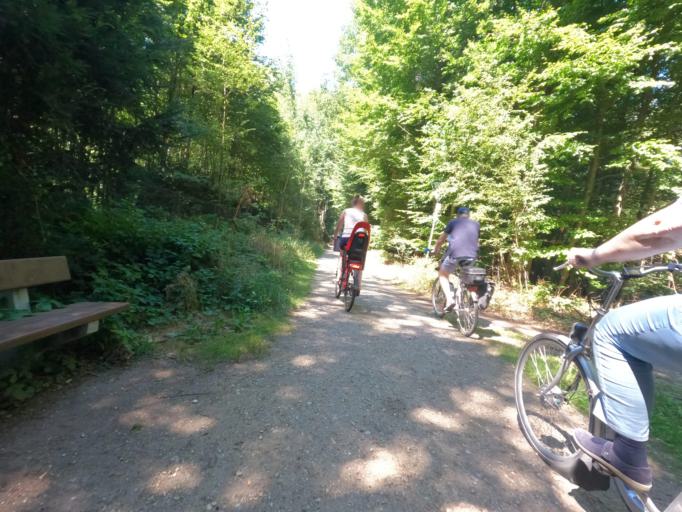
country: DE
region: North Rhine-Westphalia
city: Wegberg
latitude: 51.1482
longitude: 6.3024
